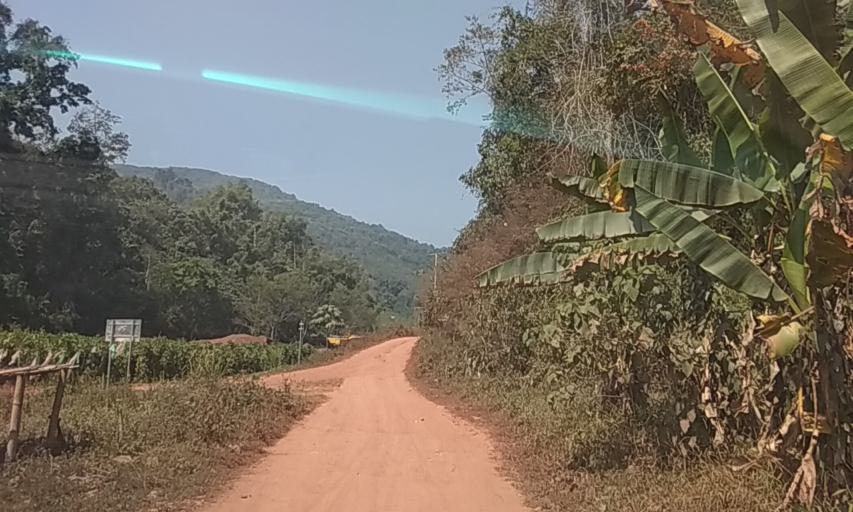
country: CN
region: Yunnan
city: Mengla
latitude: 21.5337
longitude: 101.8315
